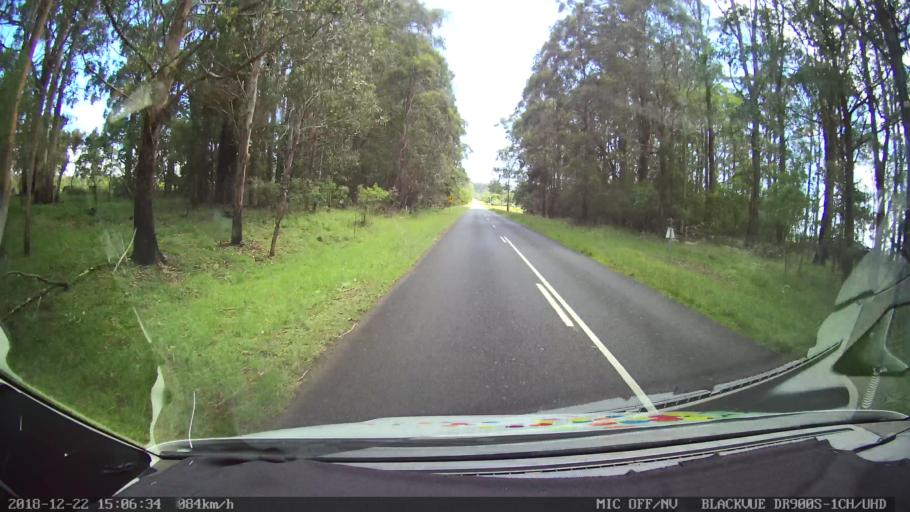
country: AU
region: New South Wales
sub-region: Bellingen
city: Dorrigo
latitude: -30.2945
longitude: 152.4256
